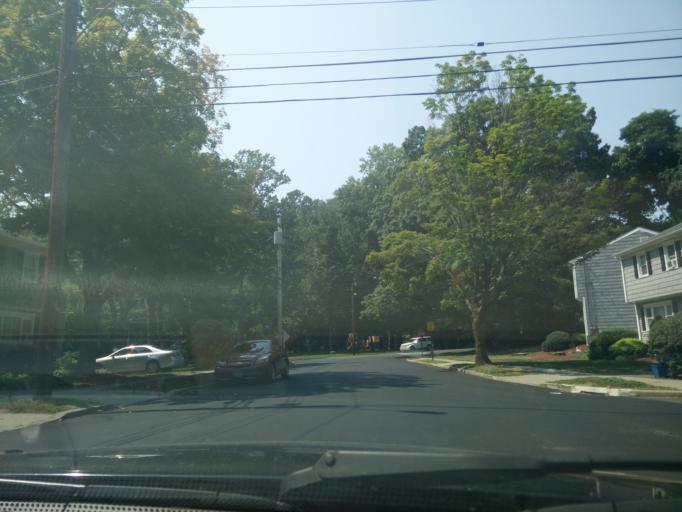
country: US
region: Connecticut
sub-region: Fairfield County
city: Fairfield
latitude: 41.1625
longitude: -73.2417
